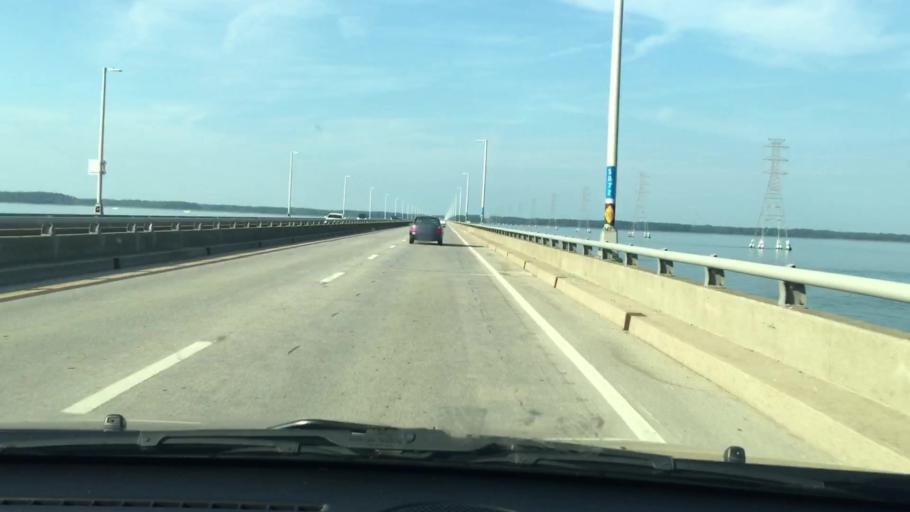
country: US
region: Virginia
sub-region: City of Newport News
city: Newport News
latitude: 36.9889
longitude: -76.4858
